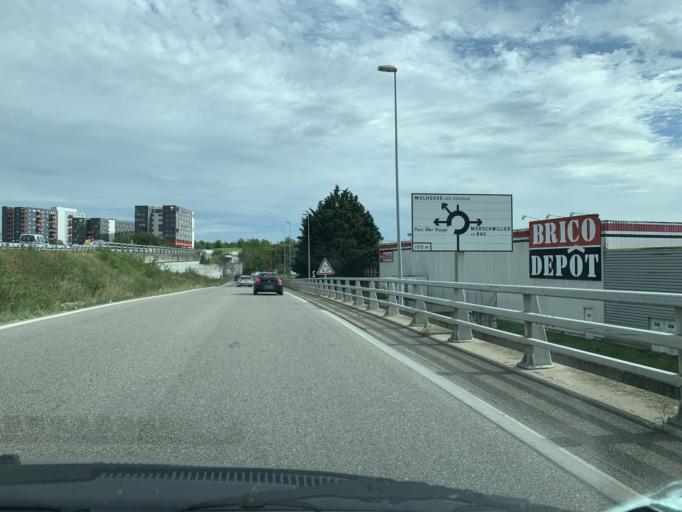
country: FR
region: Alsace
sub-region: Departement du Haut-Rhin
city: Morschwiller-le-Bas
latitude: 47.7386
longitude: 7.2876
